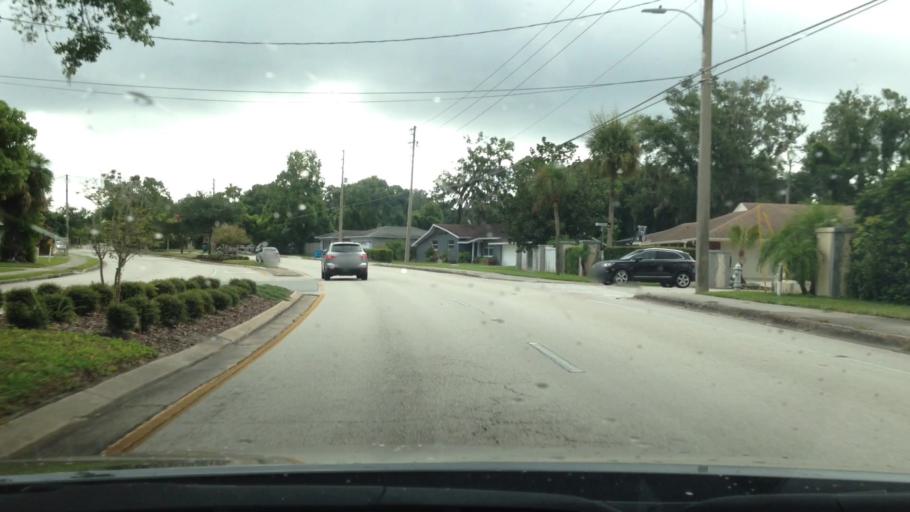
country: US
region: Florida
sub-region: Orange County
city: Maitland
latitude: 28.6271
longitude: -81.3532
